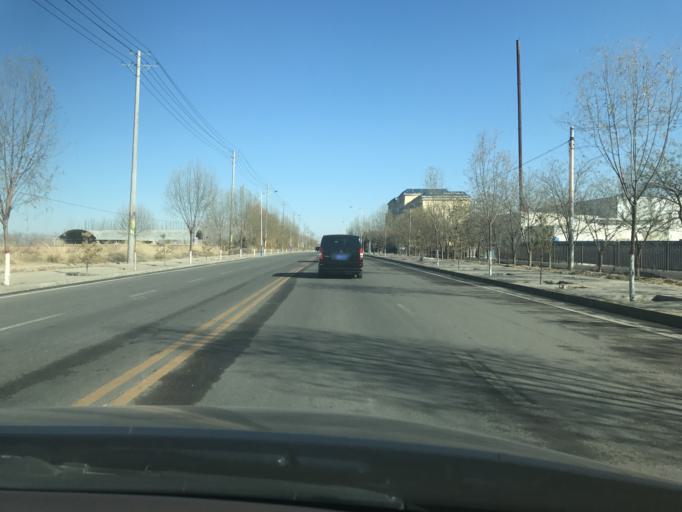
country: CN
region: Gansu Sheng
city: Gulang
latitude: 37.6856
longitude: 102.8388
